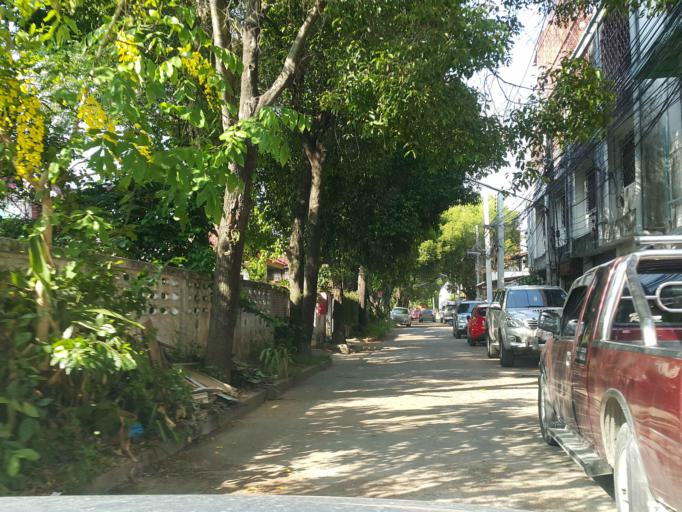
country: TH
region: Chiang Mai
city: Chiang Mai
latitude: 18.7677
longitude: 98.9964
